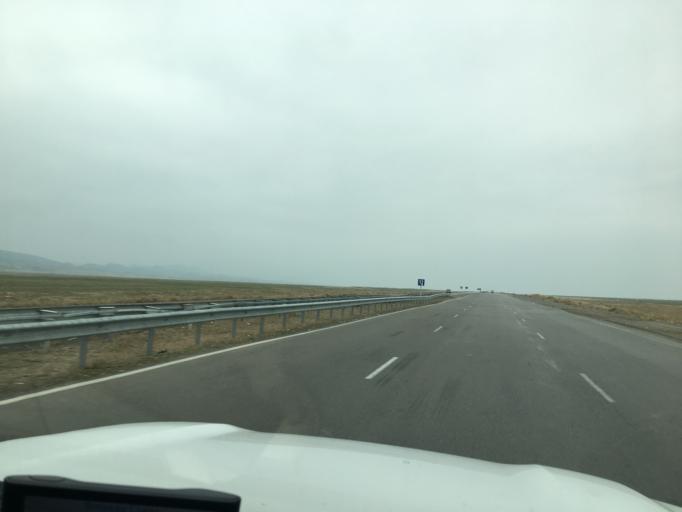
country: IR
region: Razavi Khorasan
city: Dargaz
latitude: 37.6960
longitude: 59.0510
